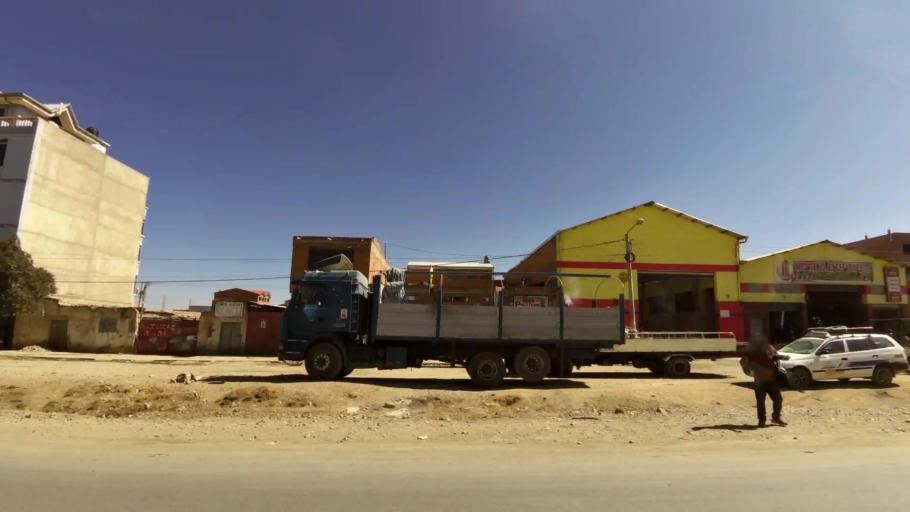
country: BO
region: La Paz
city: La Paz
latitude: -16.5405
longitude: -68.1960
